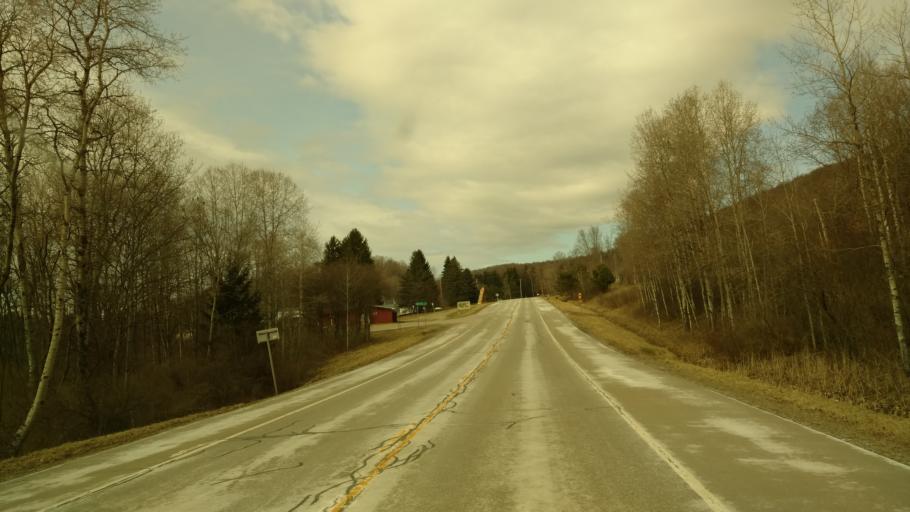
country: US
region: New York
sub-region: Allegany County
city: Wellsville
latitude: 42.0237
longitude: -77.8982
